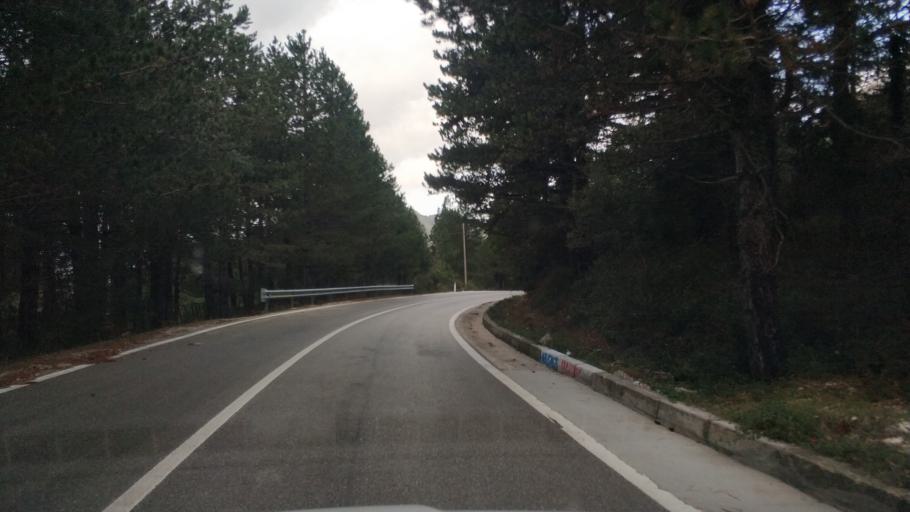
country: AL
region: Vlore
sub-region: Rrethi i Vlores
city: Brataj
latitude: 40.2247
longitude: 19.5784
